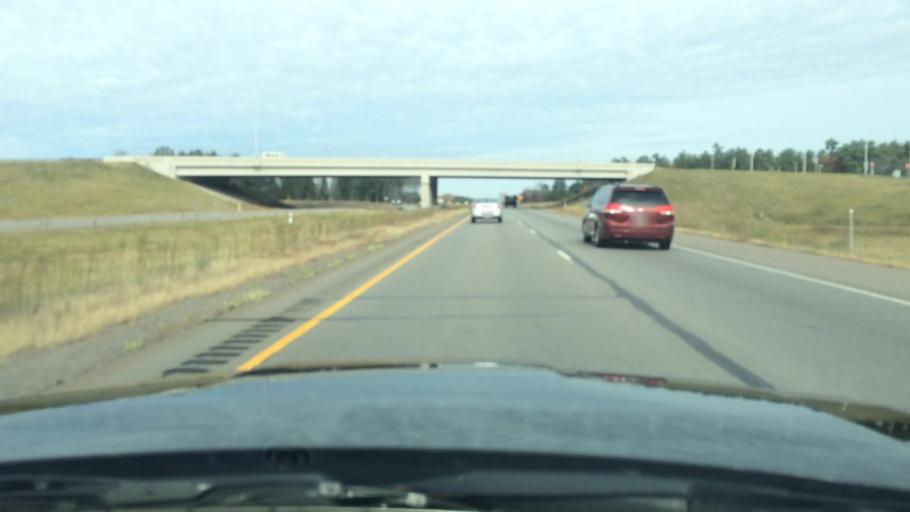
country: US
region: Wisconsin
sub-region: Marathon County
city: Mosinee
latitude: 44.8102
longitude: -89.6732
